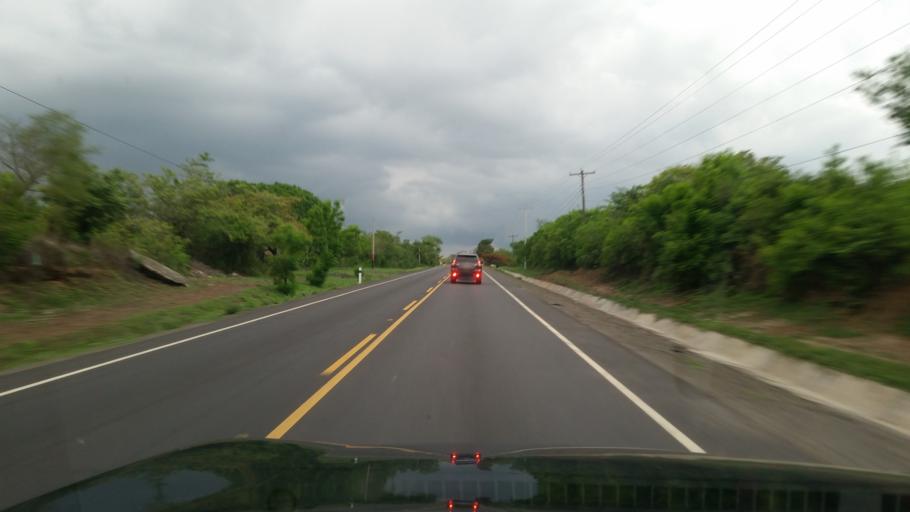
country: NI
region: Leon
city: Nagarote
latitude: 12.2689
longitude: -86.5526
